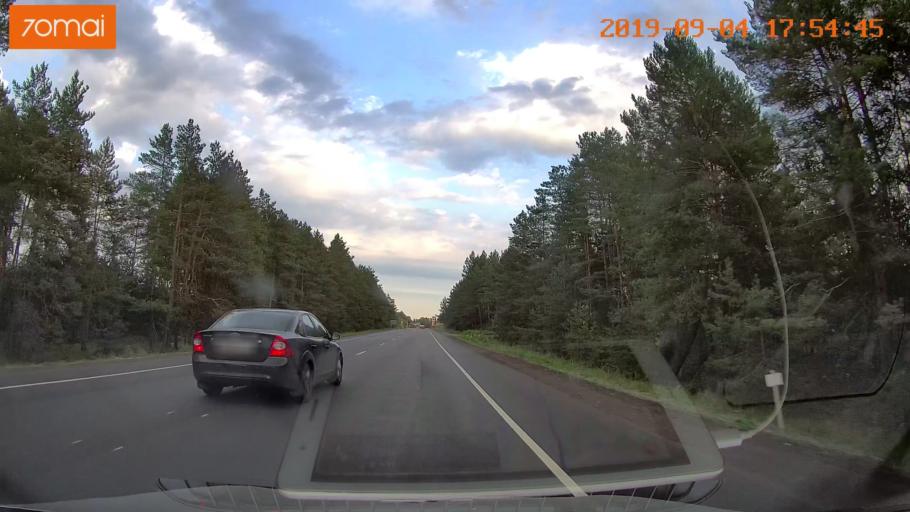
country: RU
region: Moskovskaya
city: Imeni Tsyurupy
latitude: 55.5089
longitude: 38.7536
